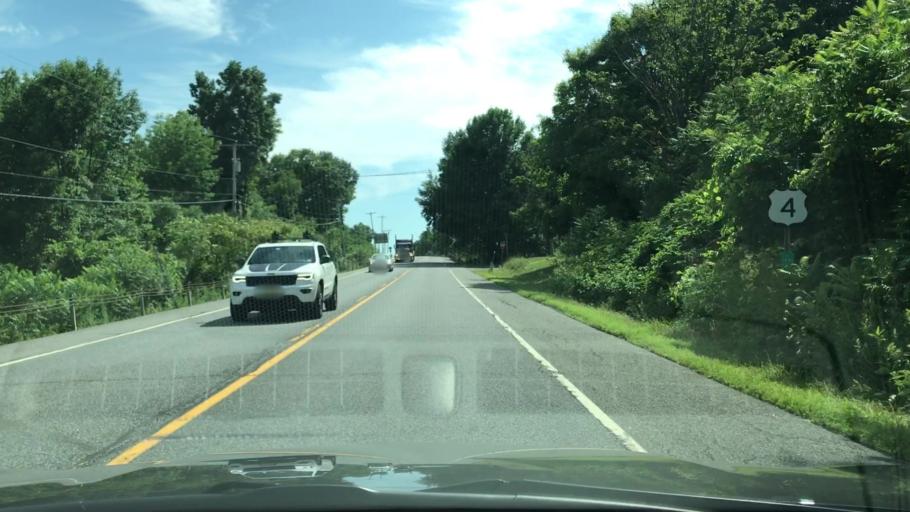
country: US
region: Vermont
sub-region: Rutland County
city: Fair Haven
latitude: 43.5808
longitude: -73.3073
